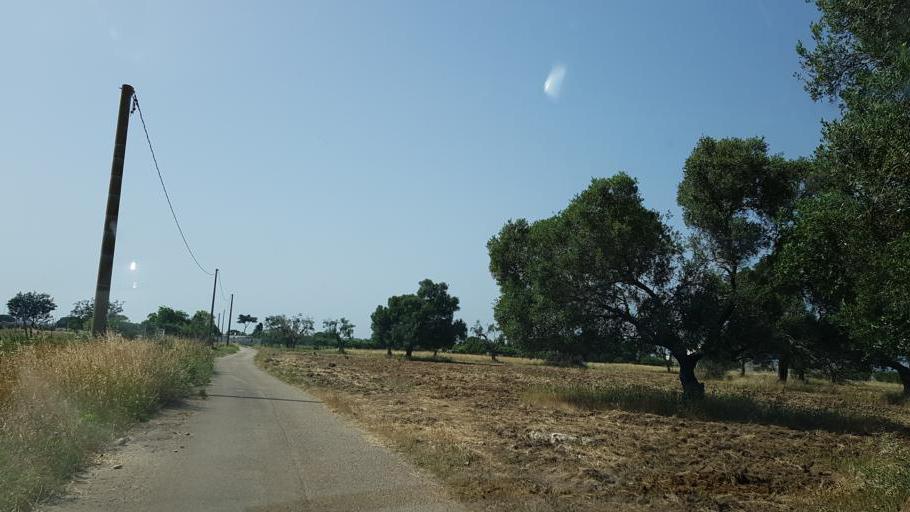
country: IT
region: Apulia
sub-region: Provincia di Brindisi
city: Brindisi
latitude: 40.6614
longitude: 17.9264
